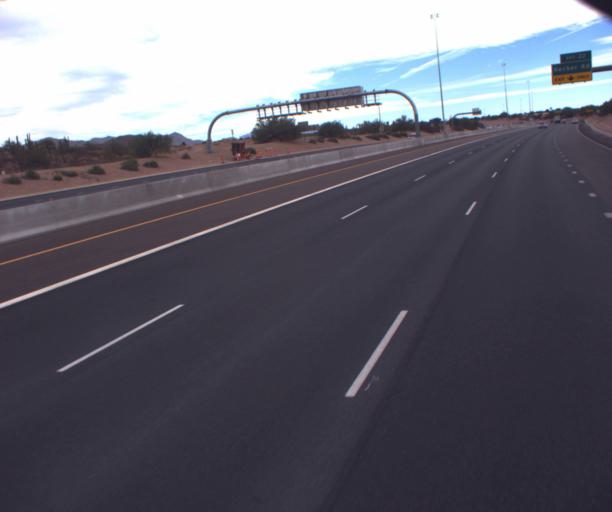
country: US
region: Arizona
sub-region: Maricopa County
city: Mesa
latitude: 33.4791
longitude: -111.7120
